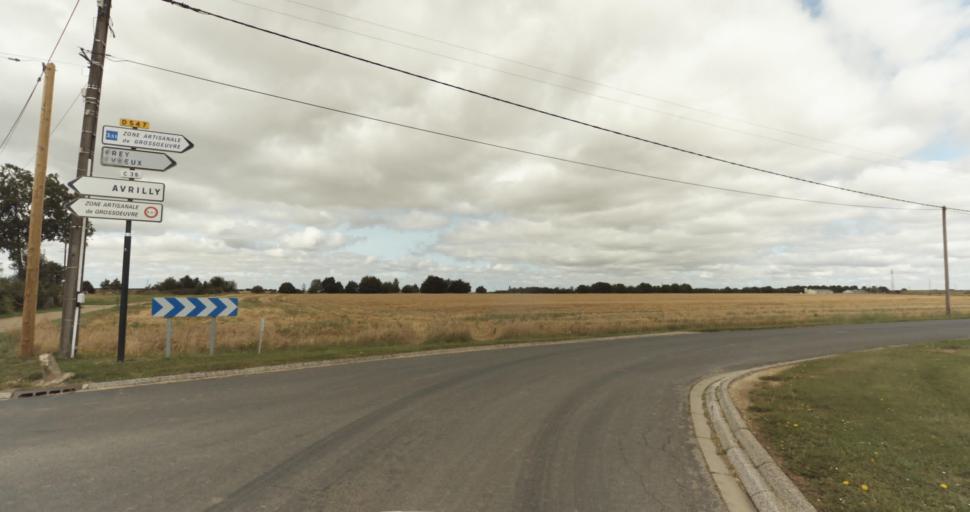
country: FR
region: Haute-Normandie
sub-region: Departement de l'Eure
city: Evreux
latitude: 48.9427
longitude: 1.1968
